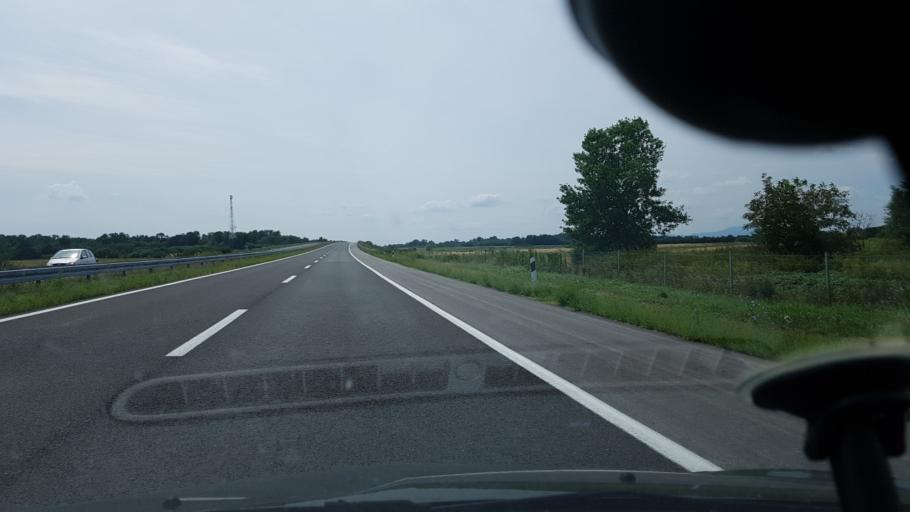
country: HR
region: Medimurska
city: Palovec
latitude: 46.3819
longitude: 16.5549
